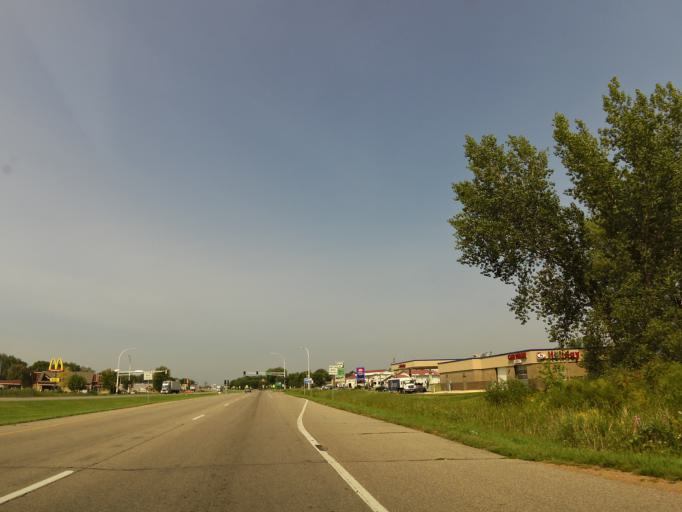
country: US
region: Minnesota
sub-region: Carver County
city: Norwood Young America
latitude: 44.7709
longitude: -93.9178
